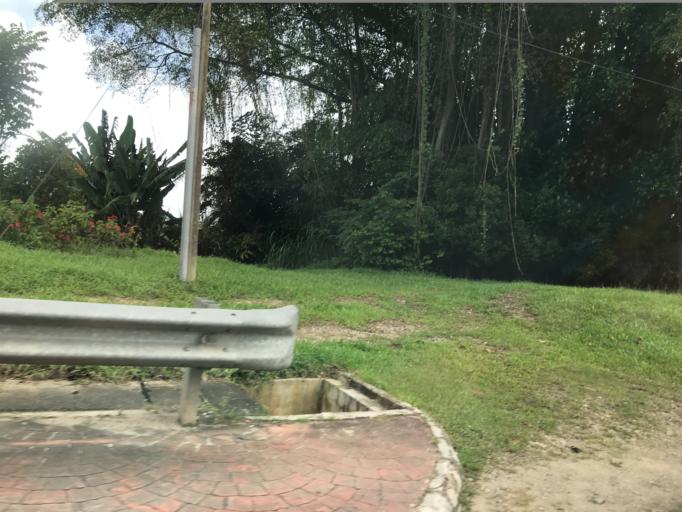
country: MY
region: Johor
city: Taman Senai
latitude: 1.6041
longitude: 103.6474
